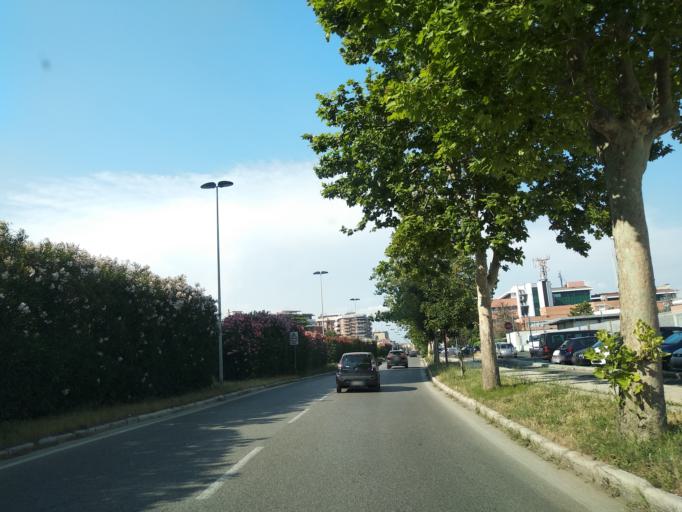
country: IT
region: Tuscany
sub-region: Provincia di Livorno
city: Livorno
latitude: 43.5384
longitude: 10.3228
